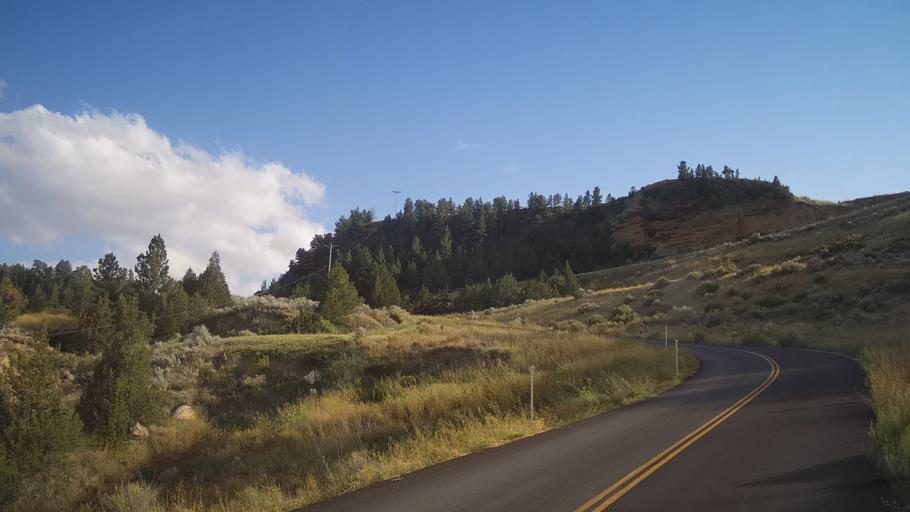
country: US
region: Montana
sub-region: Dawson County
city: Glendive
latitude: 47.0634
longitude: -104.6814
